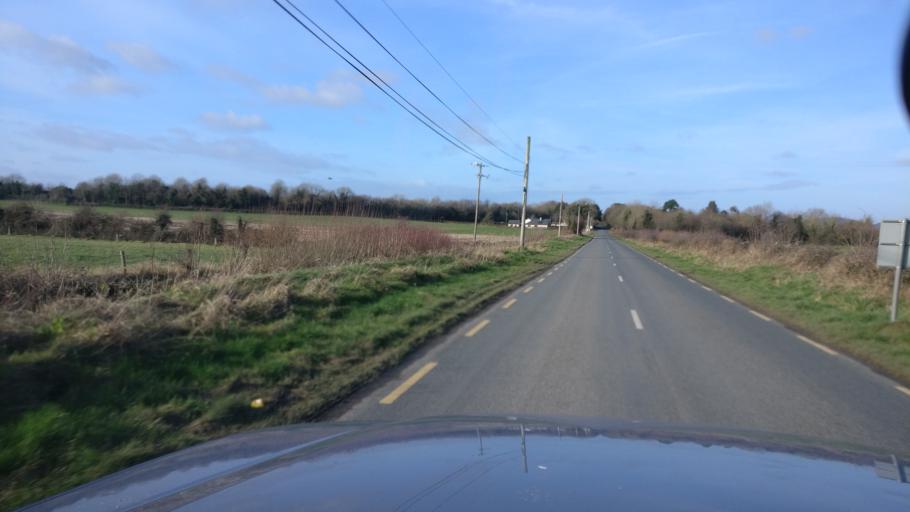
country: IE
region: Leinster
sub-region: Laois
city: Stradbally
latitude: 52.9633
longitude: -7.2035
